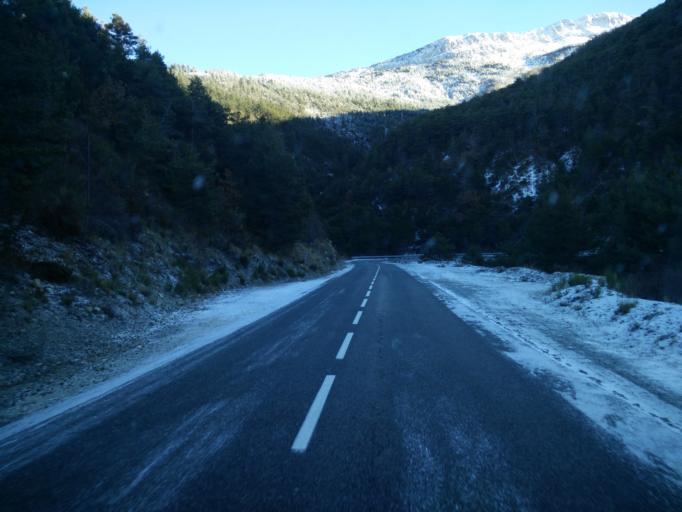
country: FR
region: Provence-Alpes-Cote d'Azur
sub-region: Departement des Alpes-de-Haute-Provence
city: Castellane
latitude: 43.8956
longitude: 6.5386
